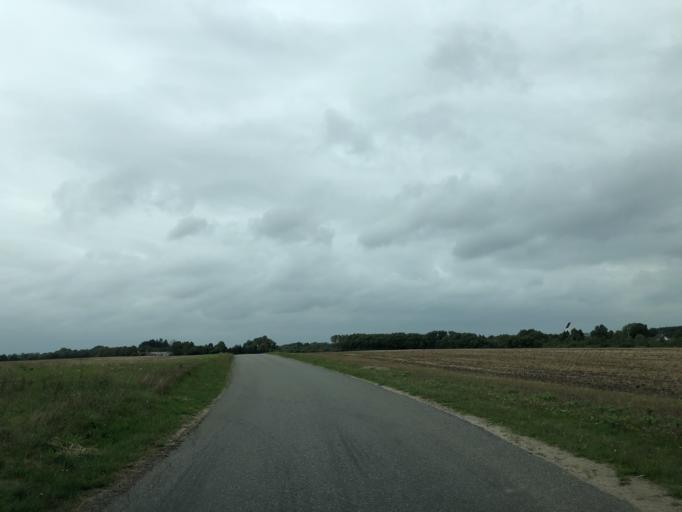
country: DK
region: Central Jutland
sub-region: Herning Kommune
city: Lind
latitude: 56.0858
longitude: 8.9554
